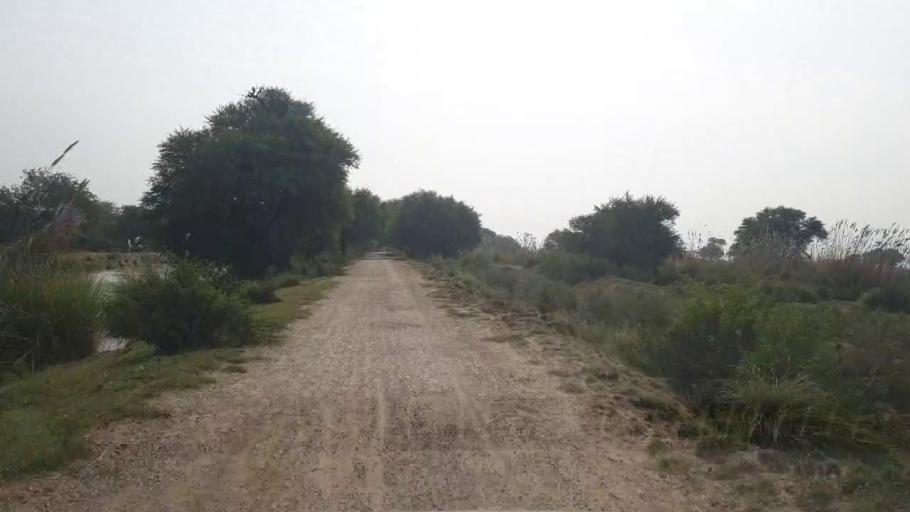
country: PK
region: Sindh
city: Tando Muhammad Khan
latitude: 25.1239
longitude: 68.4371
